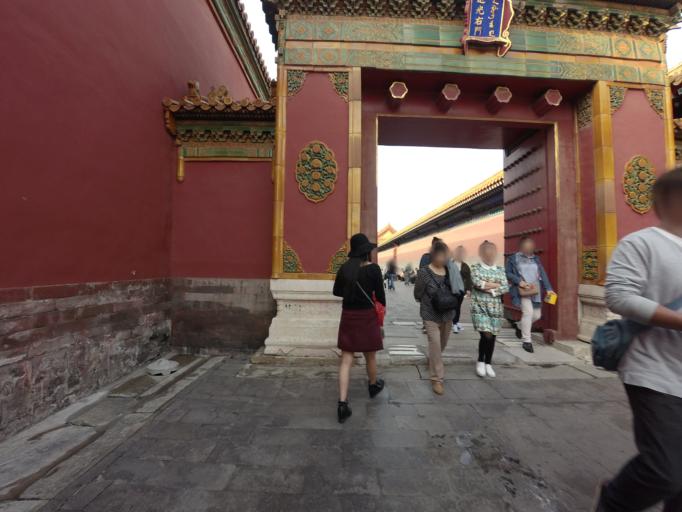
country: CN
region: Beijing
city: Beijing
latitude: 39.9184
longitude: 116.3899
